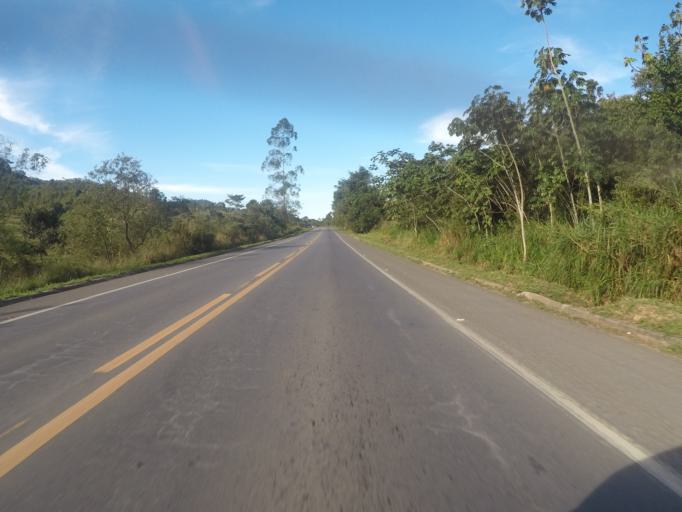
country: BR
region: Espirito Santo
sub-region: Ibiracu
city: Ibiracu
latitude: -19.8671
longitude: -40.4009
